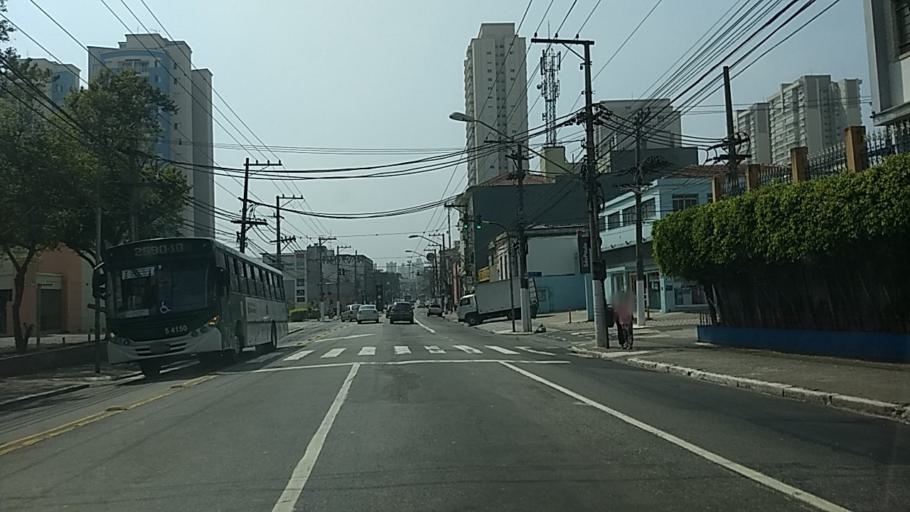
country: BR
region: Sao Paulo
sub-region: Sao Paulo
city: Sao Paulo
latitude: -23.5372
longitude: -46.5940
